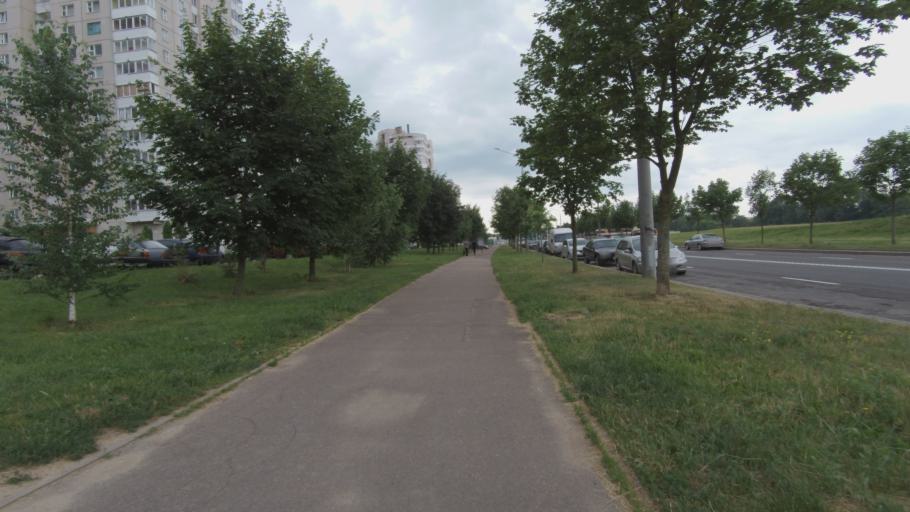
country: BY
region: Minsk
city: Syenitsa
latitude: 53.8485
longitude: 27.5593
